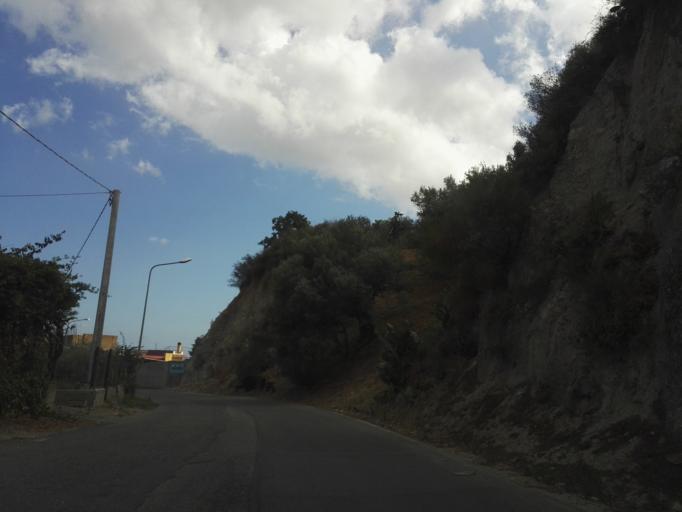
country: IT
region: Calabria
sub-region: Provincia di Reggio Calabria
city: Riace
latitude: 38.4212
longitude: 16.4815
